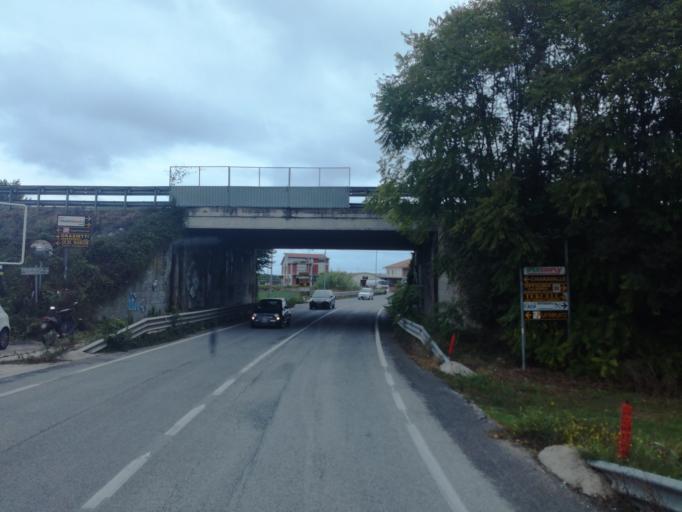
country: IT
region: The Marches
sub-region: Provincia di Ancona
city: Camerata Picena
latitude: 43.5980
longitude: 13.3560
